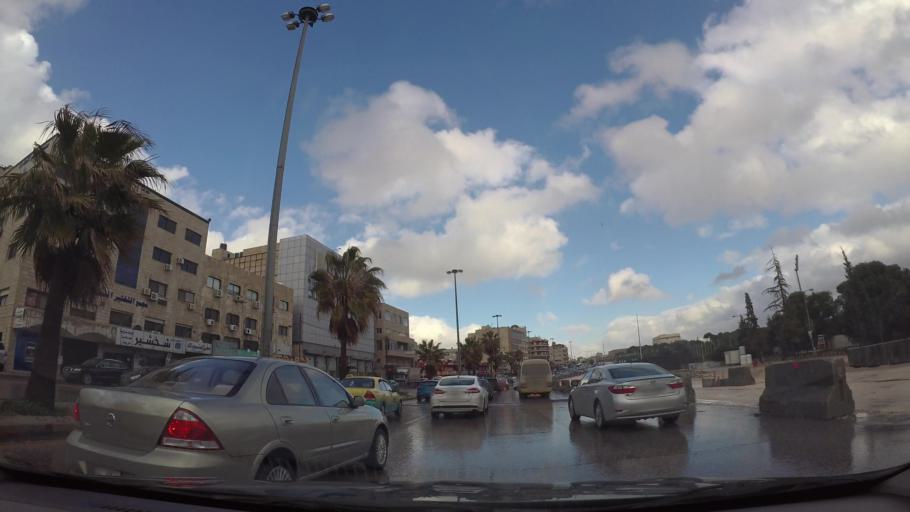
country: JO
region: Amman
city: Al Jubayhah
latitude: 31.9871
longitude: 35.9006
